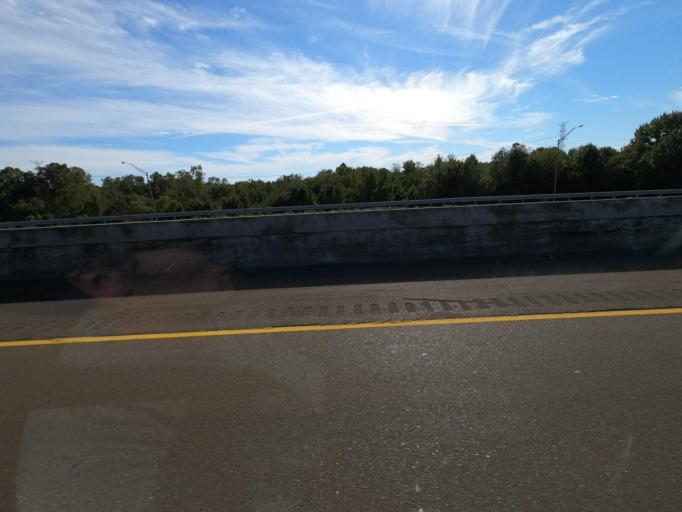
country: US
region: Tennessee
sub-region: Shelby County
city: Germantown
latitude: 35.0676
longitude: -89.8456
